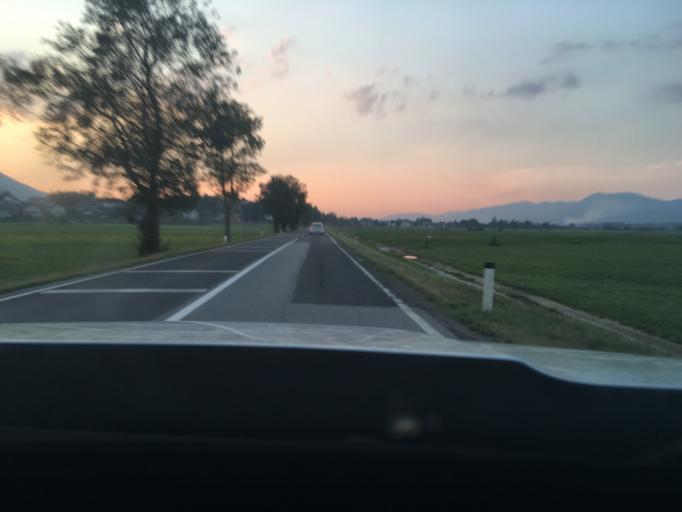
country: SI
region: Ribnica
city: Ribnica
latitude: 45.6994
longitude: 14.7614
